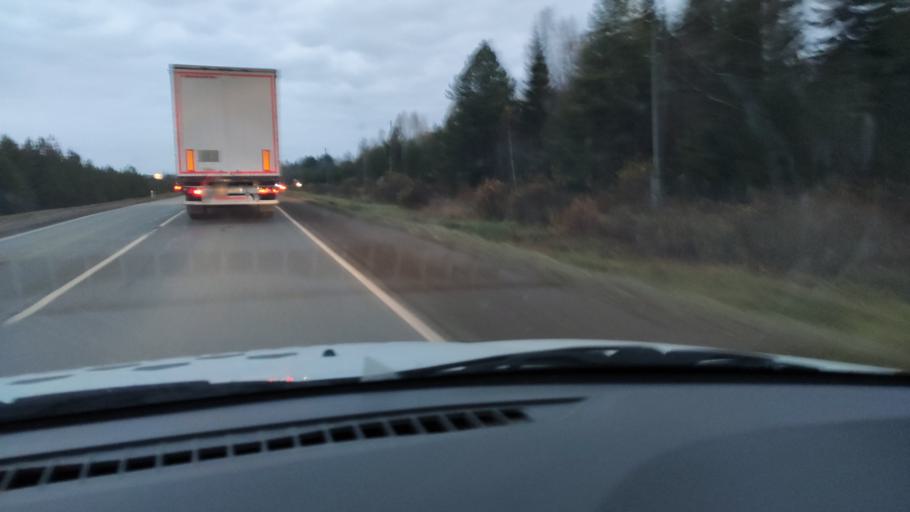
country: RU
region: Kirov
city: Kostino
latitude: 58.8547
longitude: 53.2065
